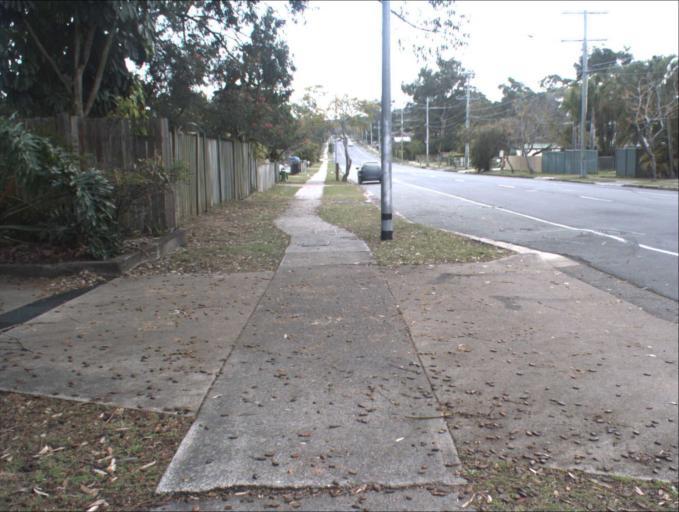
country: AU
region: Queensland
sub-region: Logan
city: Waterford West
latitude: -27.6804
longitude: 153.1000
